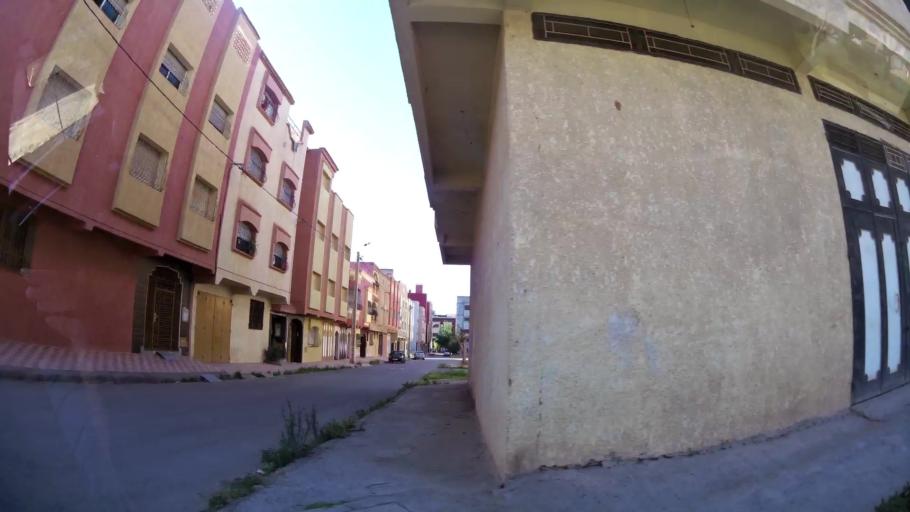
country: MA
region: Oriental
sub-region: Berkane-Taourirt
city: Berkane
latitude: 34.9309
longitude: -2.3410
